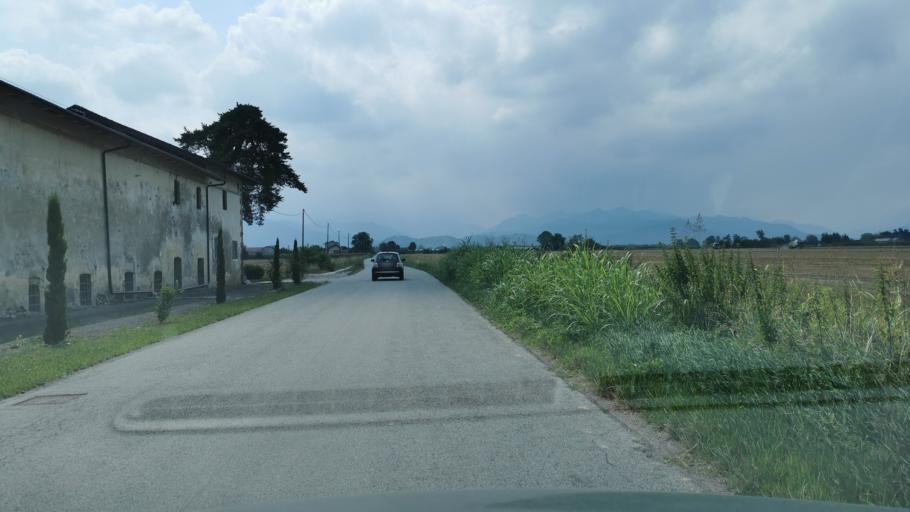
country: IT
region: Piedmont
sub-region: Provincia di Cuneo
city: San Rocco
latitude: 44.4298
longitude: 7.4814
